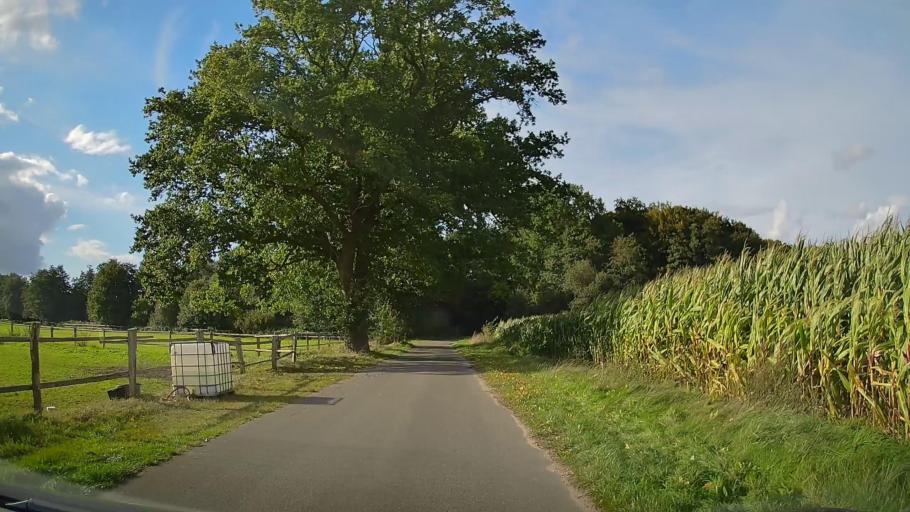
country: DE
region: Lower Saxony
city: Garlstorf
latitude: 53.2285
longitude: 10.0893
